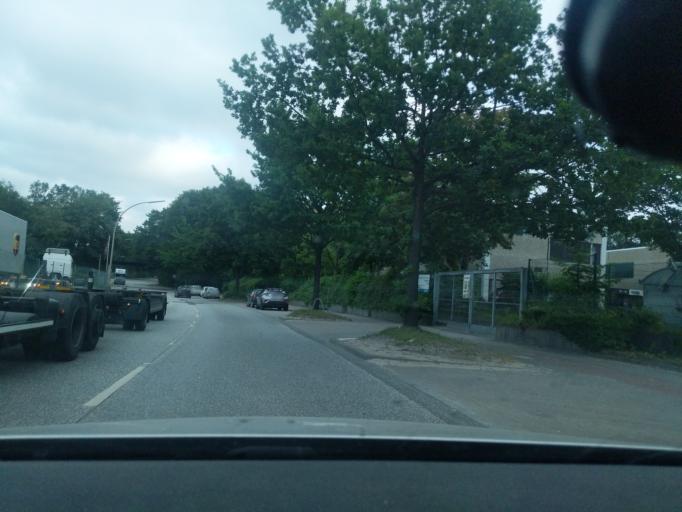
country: DE
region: Hamburg
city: Eidelstedt
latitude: 53.5871
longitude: 9.9073
